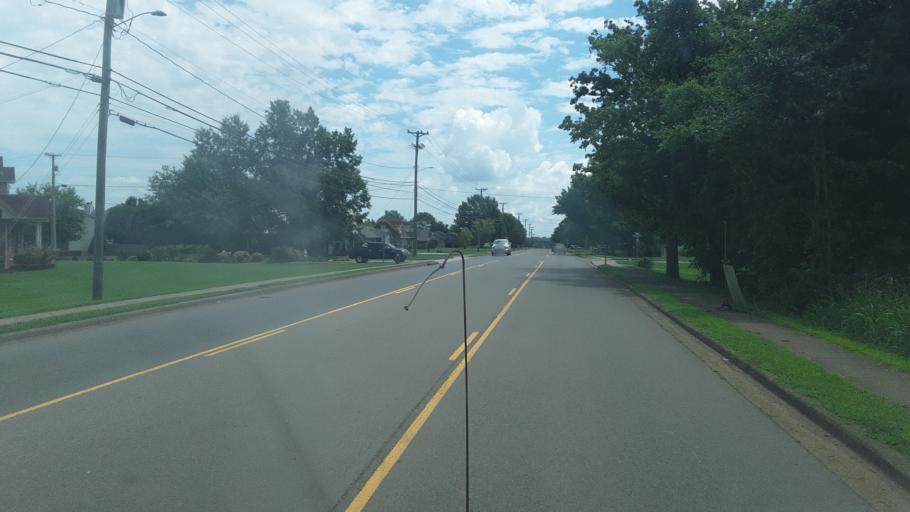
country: US
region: Tennessee
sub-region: Montgomery County
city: Clarksville
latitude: 36.5743
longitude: -87.4267
